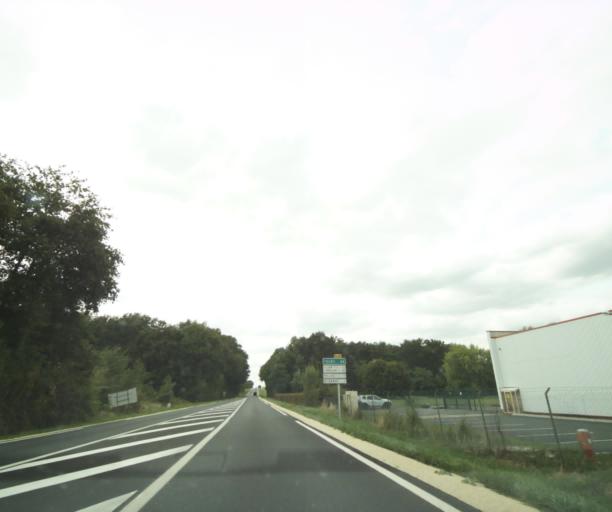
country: FR
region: Centre
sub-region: Departement de l'Indre
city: Buzancais
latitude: 46.8930
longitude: 1.3945
